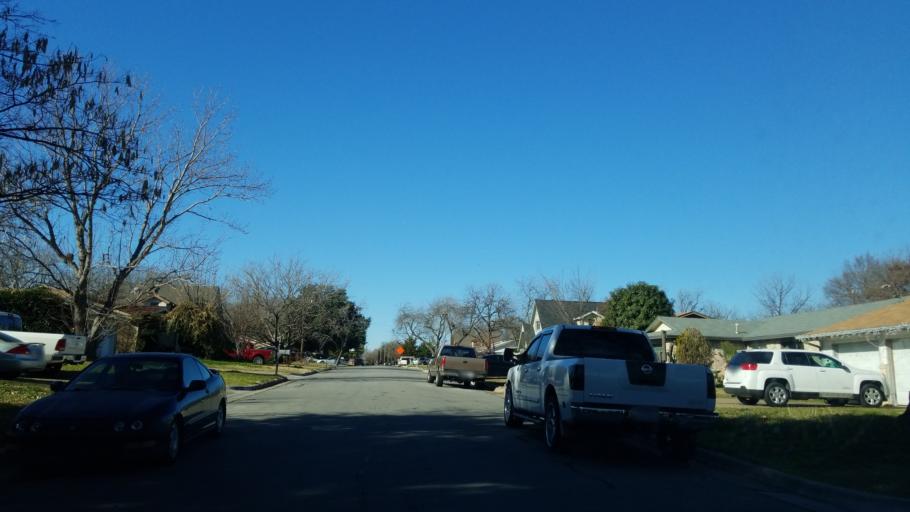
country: US
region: Texas
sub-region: Tarrant County
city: Arlington
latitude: 32.7268
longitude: -97.0589
